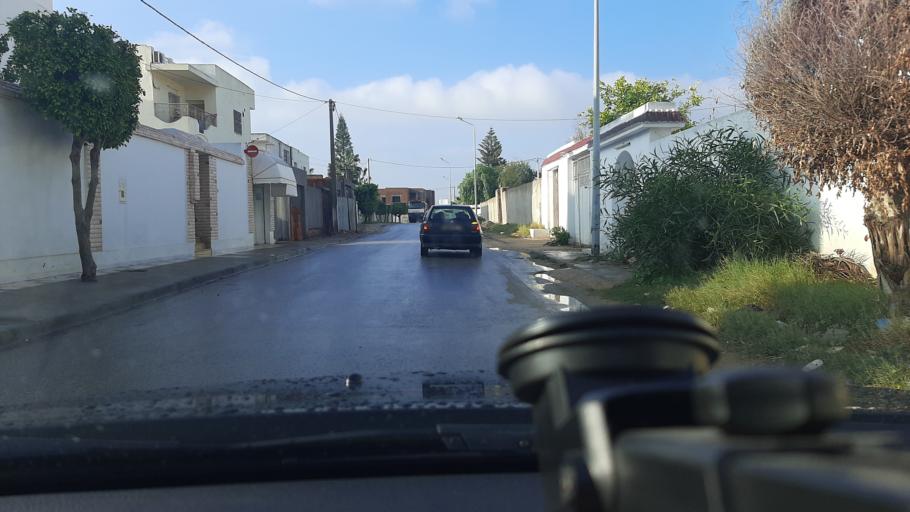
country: TN
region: Safaqis
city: Sfax
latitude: 34.7438
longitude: 10.7181
